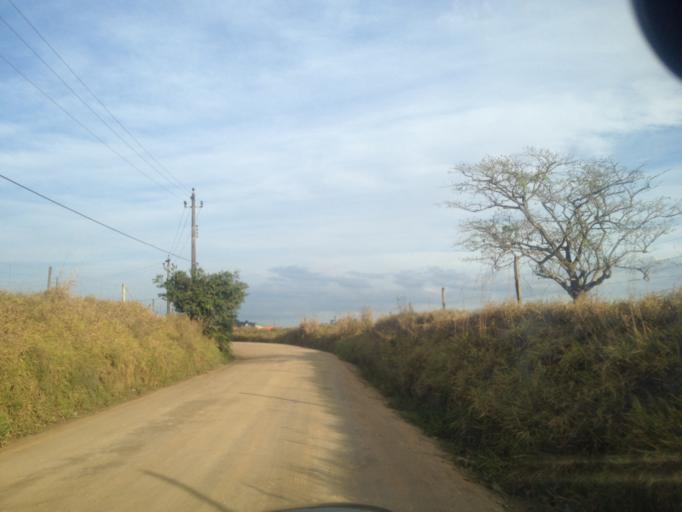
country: BR
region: Rio de Janeiro
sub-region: Quatis
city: Quatis
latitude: -22.4028
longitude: -44.2709
